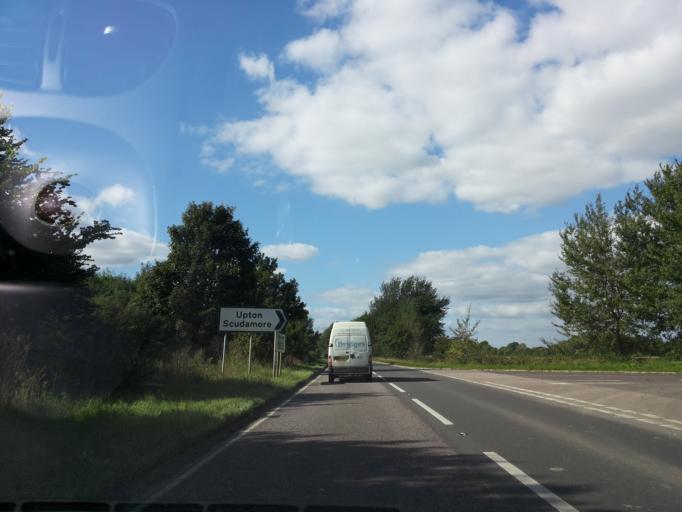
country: GB
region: England
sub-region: Wiltshire
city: Upton Scudamore
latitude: 51.2242
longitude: -2.2131
